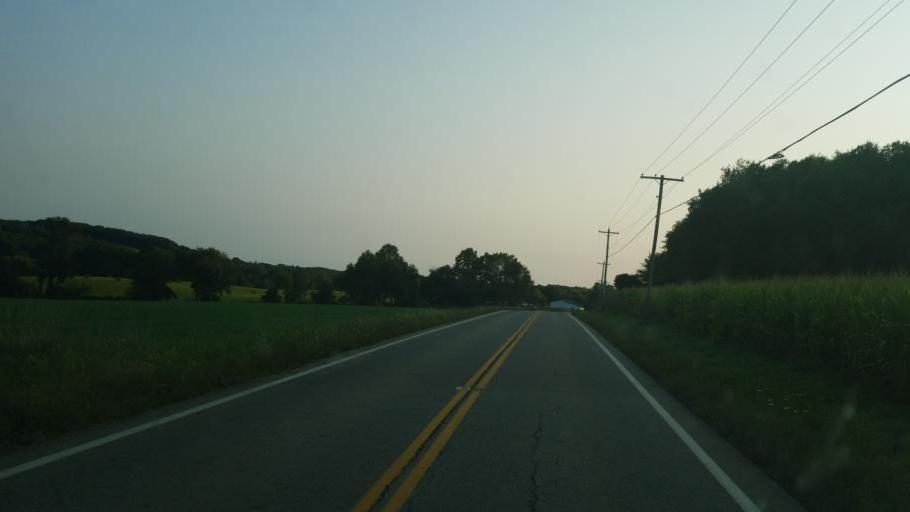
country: US
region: Ohio
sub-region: Wayne County
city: Shreve
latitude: 40.6626
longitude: -82.1190
